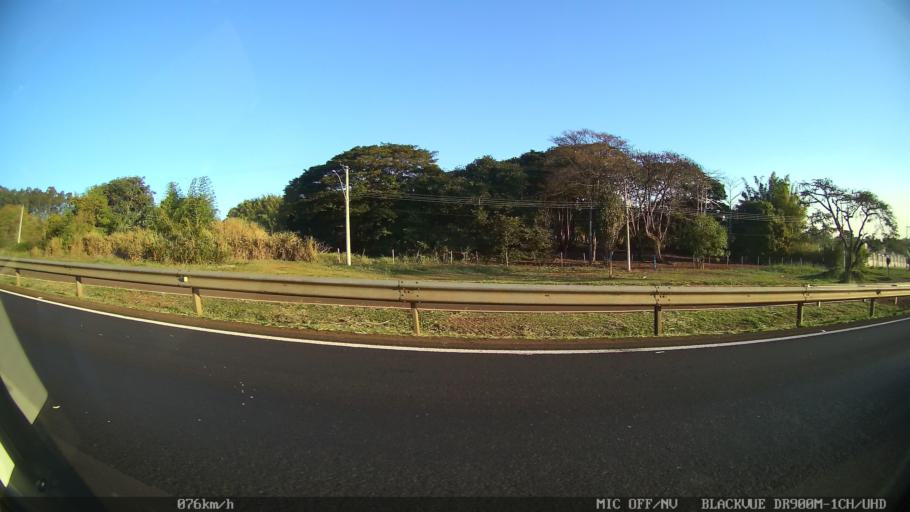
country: BR
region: Sao Paulo
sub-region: Araraquara
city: Araraquara
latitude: -21.8179
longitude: -48.1835
